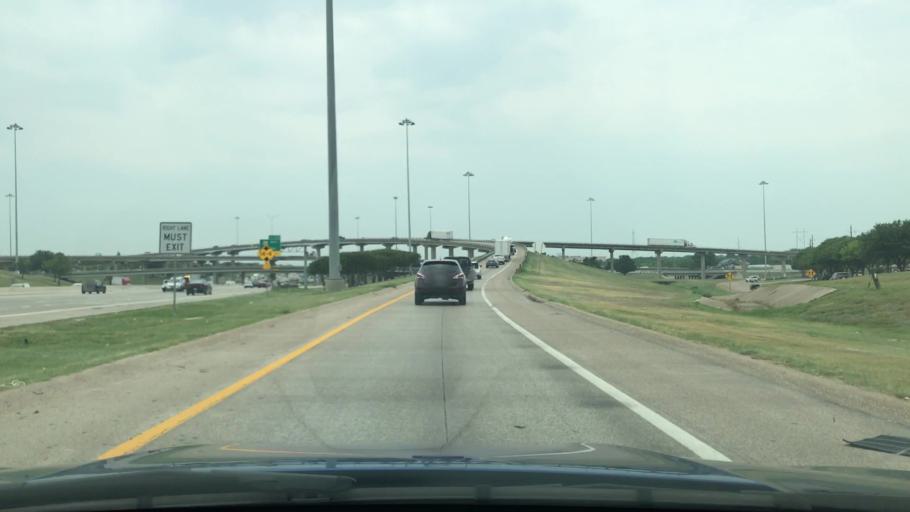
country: US
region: Texas
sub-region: Dallas County
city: Mesquite
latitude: 32.7968
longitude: -96.6261
